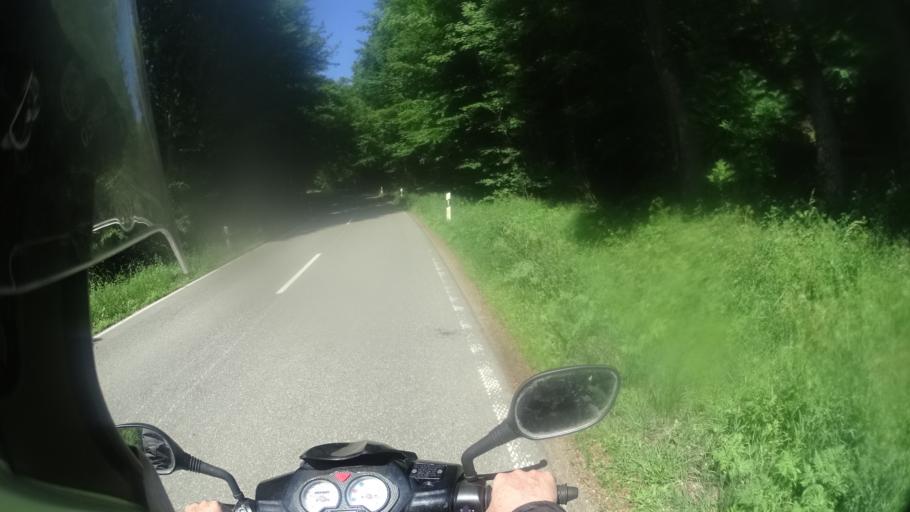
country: DE
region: Hesse
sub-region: Regierungsbezirk Darmstadt
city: Schlangenbad
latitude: 50.0885
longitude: 8.0571
